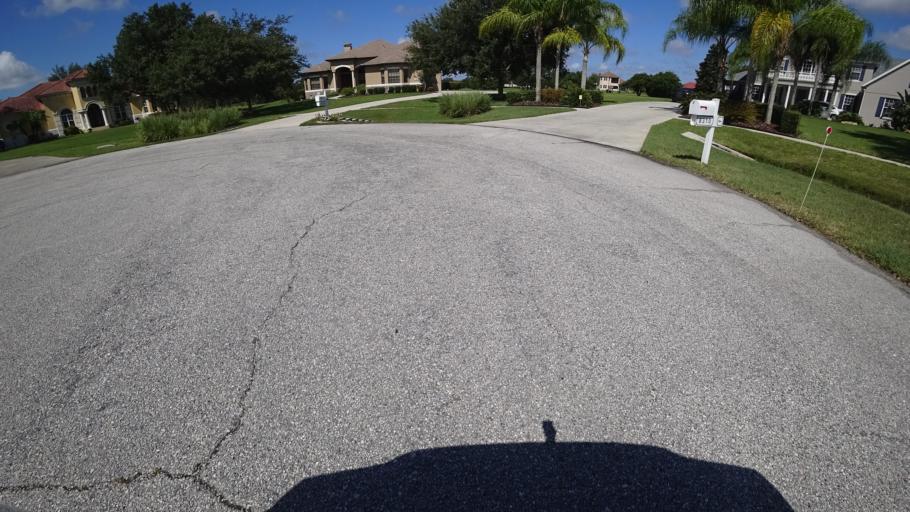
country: US
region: Florida
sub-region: Sarasota County
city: Fruitville
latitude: 27.3886
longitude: -82.3091
